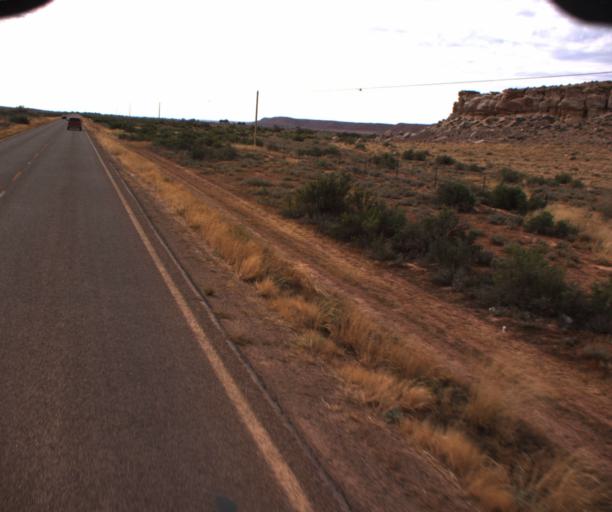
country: US
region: Arizona
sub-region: Apache County
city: Many Farms
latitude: 36.3050
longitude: -109.6084
